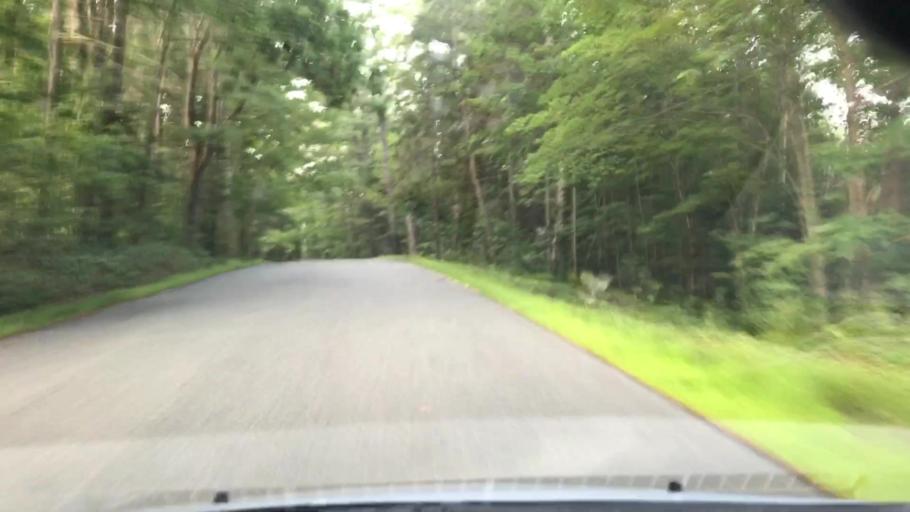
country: US
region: New Hampshire
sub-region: Grafton County
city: North Haverhill
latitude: 44.0510
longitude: -72.0079
